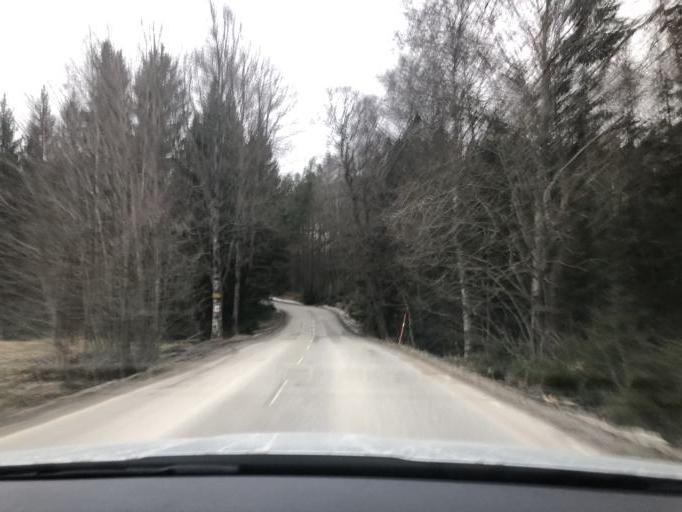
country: SE
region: Stockholm
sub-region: Botkyrka Kommun
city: Tullinge
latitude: 59.1647
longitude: 17.8965
